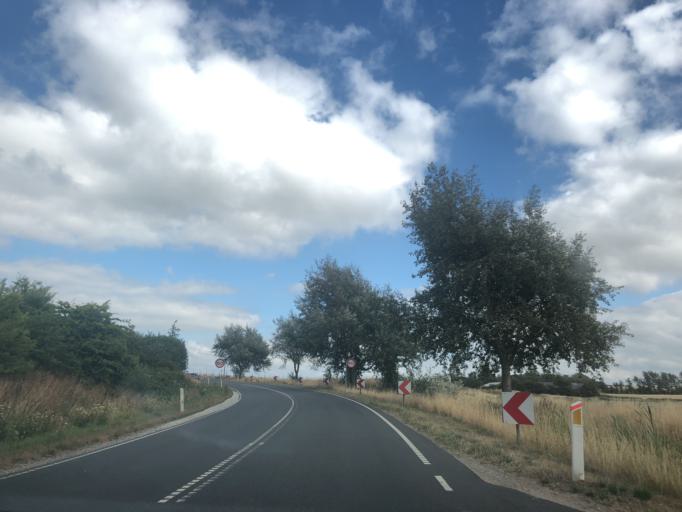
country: DK
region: Central Jutland
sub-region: Holstebro Kommune
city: Vinderup
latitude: 56.4685
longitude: 8.7012
